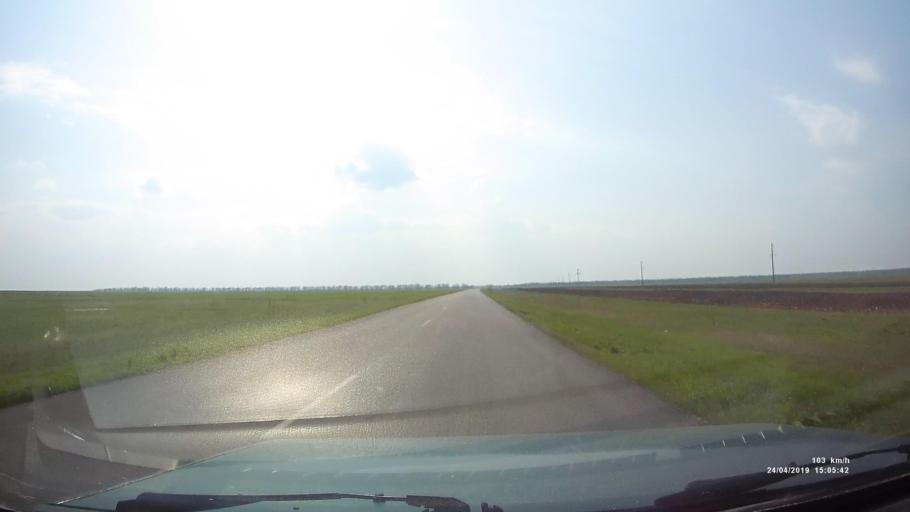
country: RU
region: Rostov
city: Remontnoye
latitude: 46.5595
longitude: 43.4431
